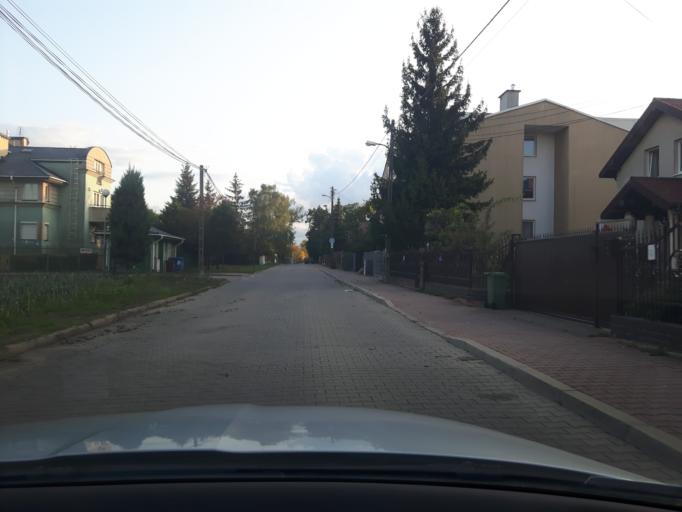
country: PL
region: Masovian Voivodeship
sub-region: Warszawa
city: Ursynow
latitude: 52.1495
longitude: 21.0220
